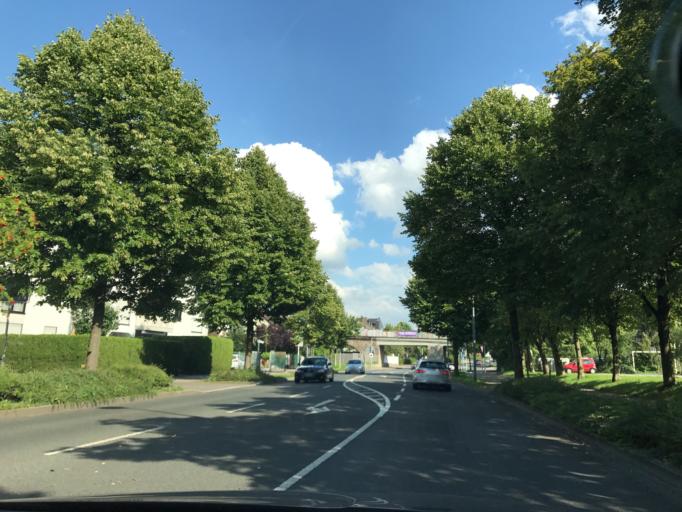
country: DE
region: North Rhine-Westphalia
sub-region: Regierungsbezirk Dusseldorf
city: Velbert
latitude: 51.3443
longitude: 7.0325
